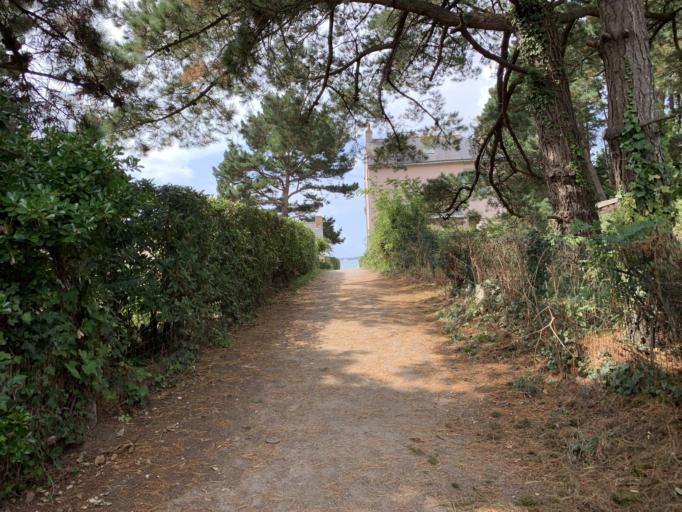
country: FR
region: Brittany
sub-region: Departement du Morbihan
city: Arradon
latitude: 47.6009
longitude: -2.8535
